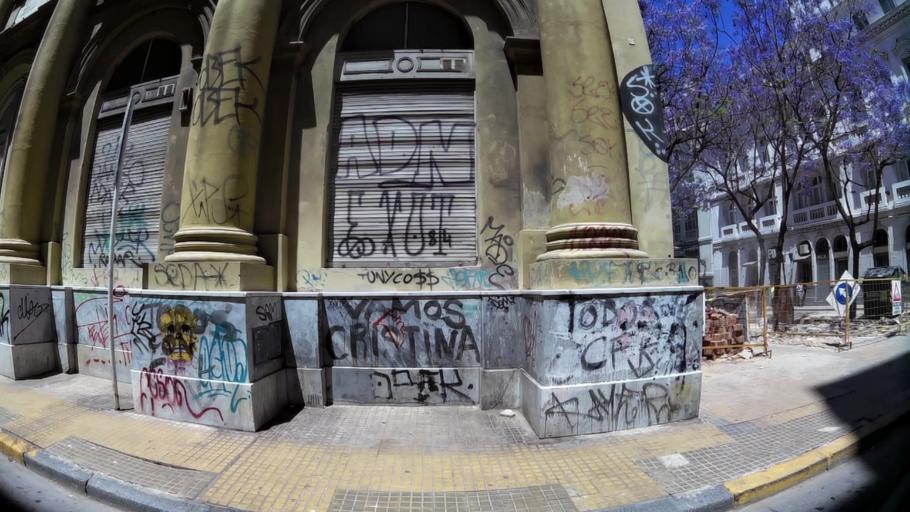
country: AR
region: Buenos Aires F.D.
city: Buenos Aires
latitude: -34.6138
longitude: -58.3745
